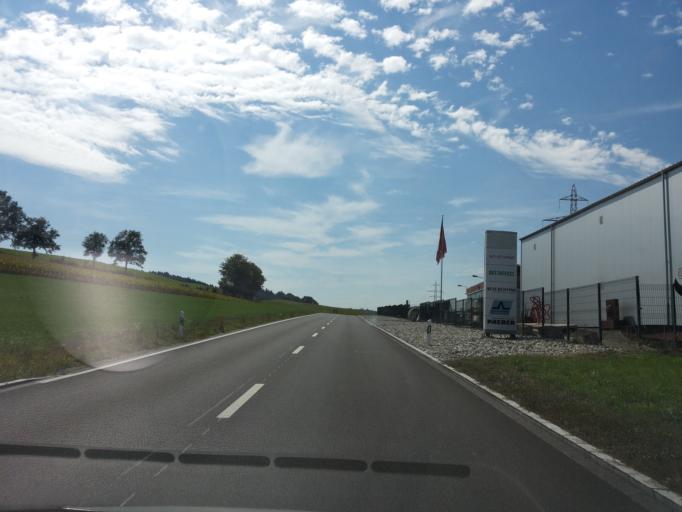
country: CH
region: Lucerne
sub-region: Willisau District
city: Pfaffnau
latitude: 47.2212
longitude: 7.8773
